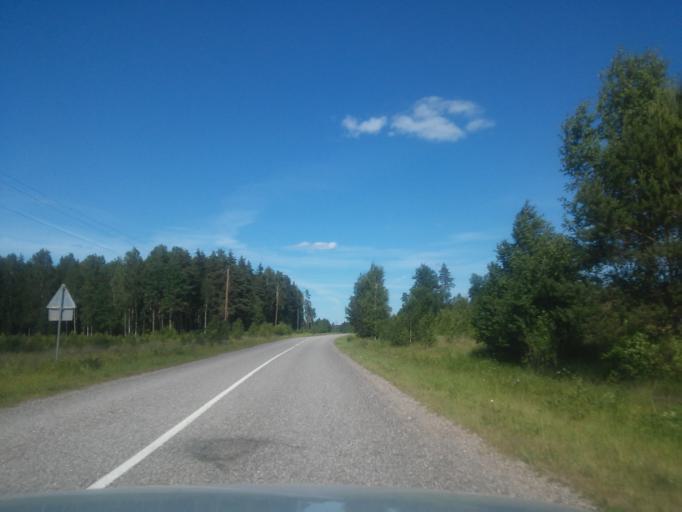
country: LV
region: Skrunda
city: Skrunda
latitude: 56.6169
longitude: 21.9531
